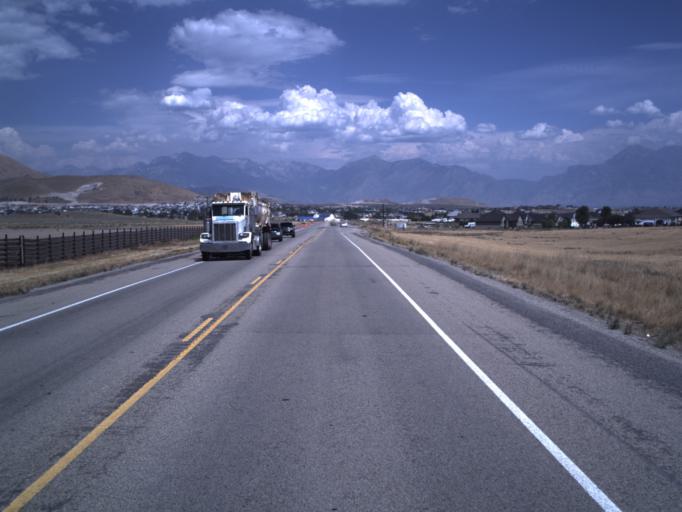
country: US
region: Utah
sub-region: Utah County
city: Eagle Mountain
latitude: 40.3712
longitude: -112.0240
